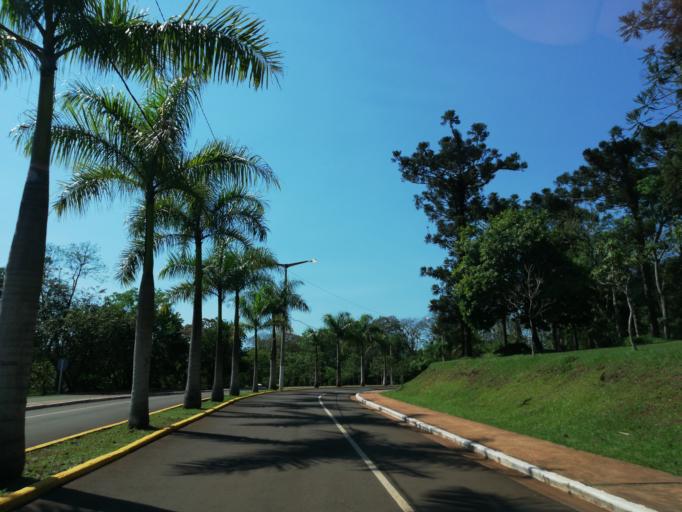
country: AR
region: Misiones
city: Puerto Eldorado
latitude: -26.4088
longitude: -54.6905
